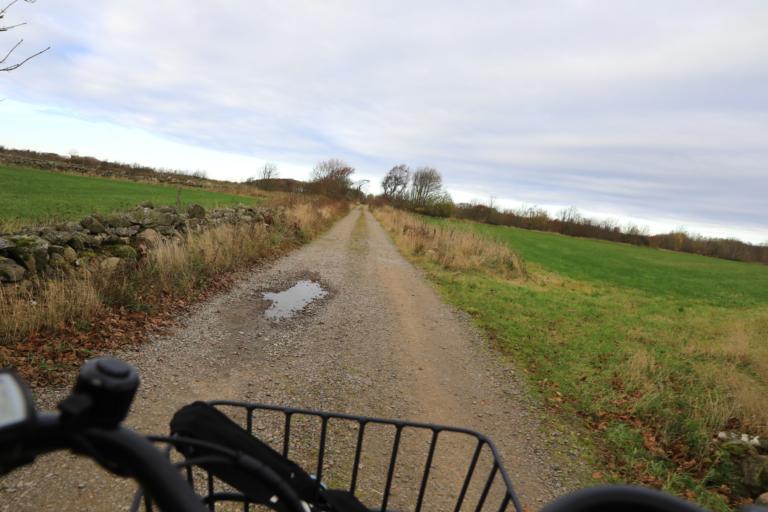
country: SE
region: Halland
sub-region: Varbergs Kommun
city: Traslovslage
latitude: 57.0551
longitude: 12.3366
